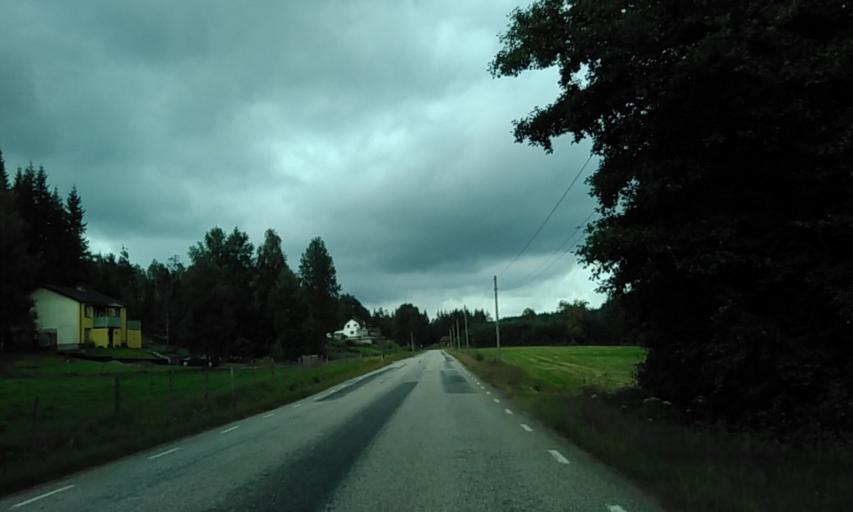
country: SE
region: Vaestra Goetaland
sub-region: Bollebygds Kommun
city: Bollebygd
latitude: 57.7380
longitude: 12.5959
